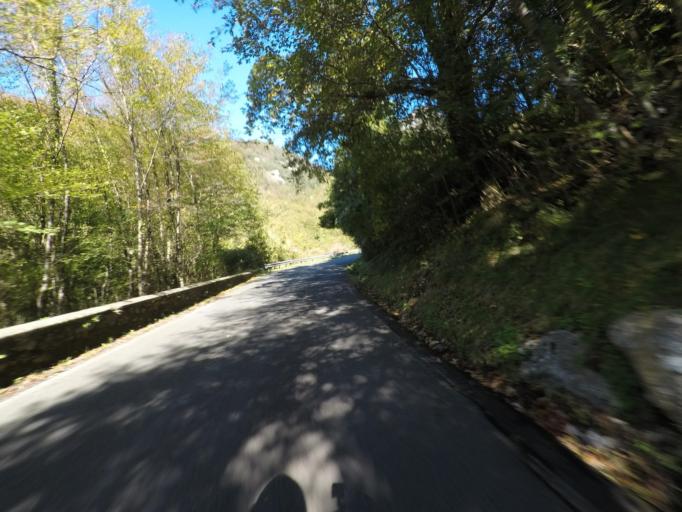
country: IT
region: Tuscany
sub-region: Provincia di Massa-Carrara
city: Carrara
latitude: 44.1098
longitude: 10.0859
